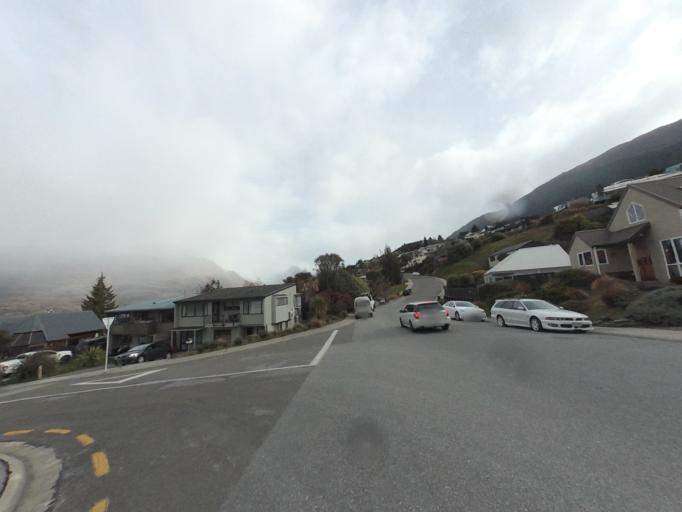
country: NZ
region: Otago
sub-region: Queenstown-Lakes District
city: Queenstown
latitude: -45.0392
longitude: 168.6378
